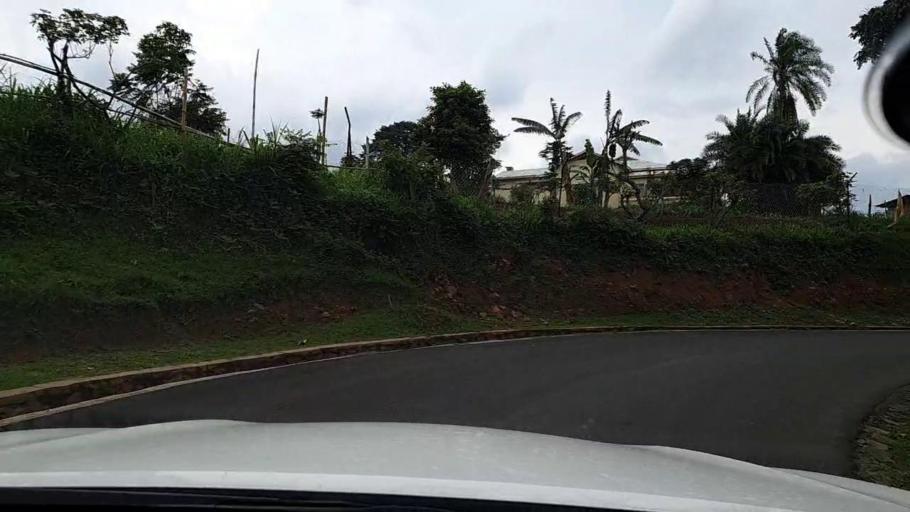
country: RW
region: Western Province
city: Kibuye
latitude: -2.1777
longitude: 29.2901
